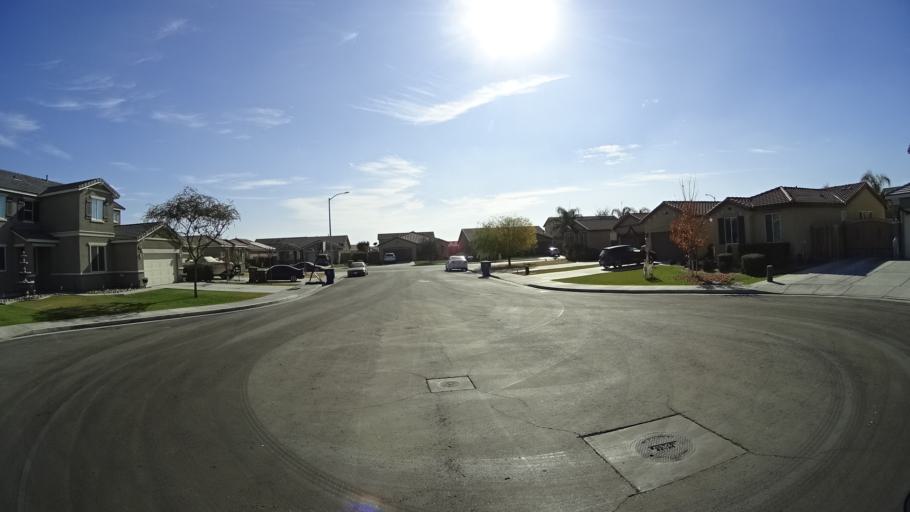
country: US
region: California
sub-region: Kern County
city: Greenfield
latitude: 35.2956
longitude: -119.0638
